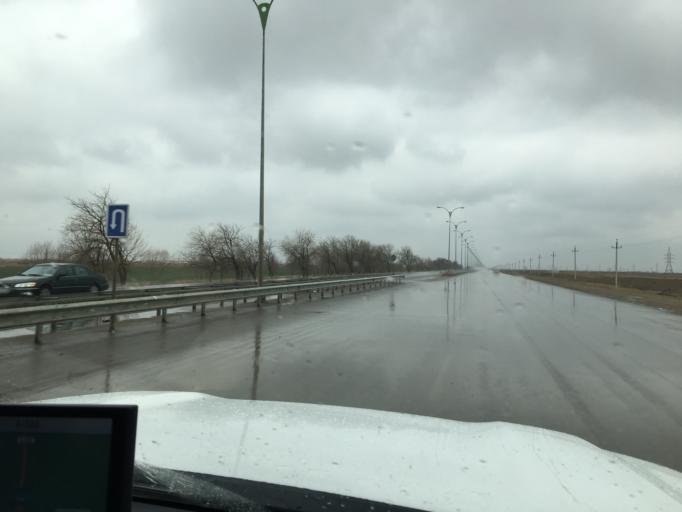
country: TM
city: Murgab
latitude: 37.5068
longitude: 61.9456
